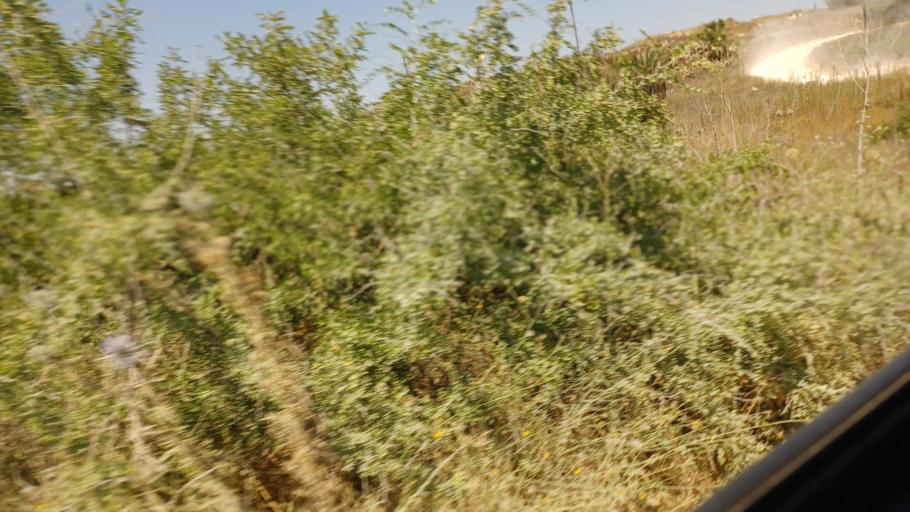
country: CY
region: Ammochostos
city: Acheritou
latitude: 35.0772
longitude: 33.8920
